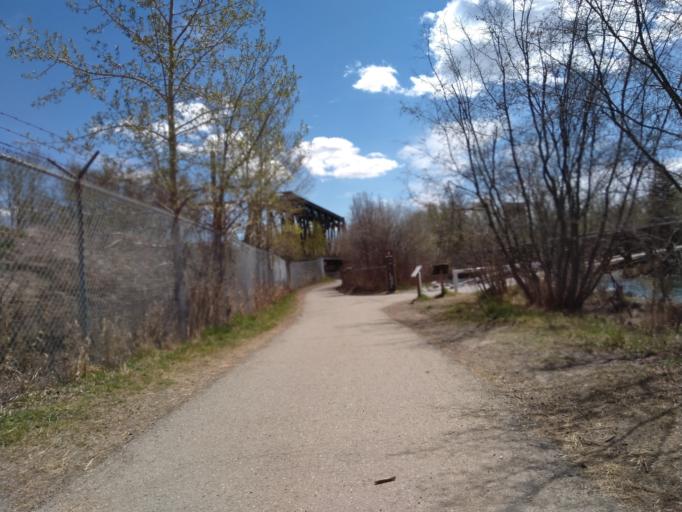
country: CA
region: Alberta
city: Calgary
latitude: 51.0997
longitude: -114.2037
